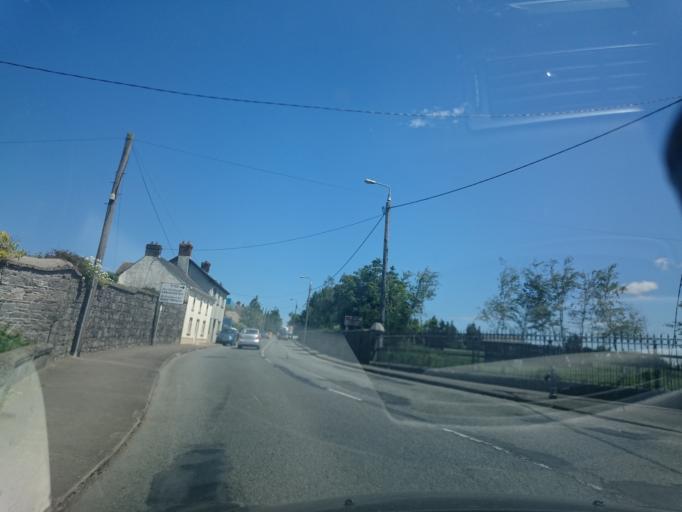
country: IE
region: Leinster
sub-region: County Carlow
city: Bagenalstown
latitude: 52.6302
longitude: -7.0623
